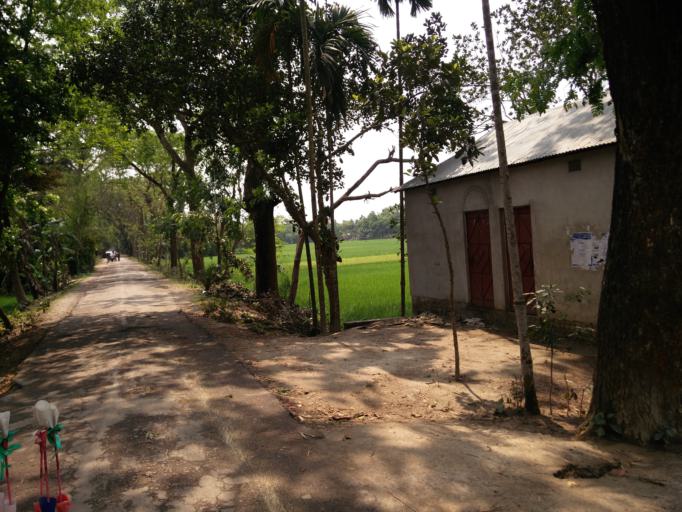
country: BD
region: Dhaka
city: Sherpur
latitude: 24.9433
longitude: 90.1602
